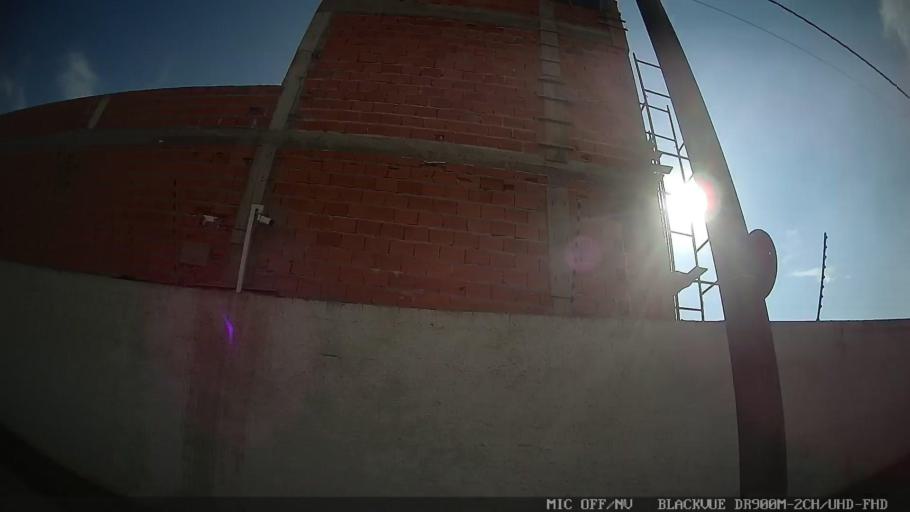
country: BR
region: Sao Paulo
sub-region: Indaiatuba
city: Indaiatuba
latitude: -23.0904
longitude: -47.2337
